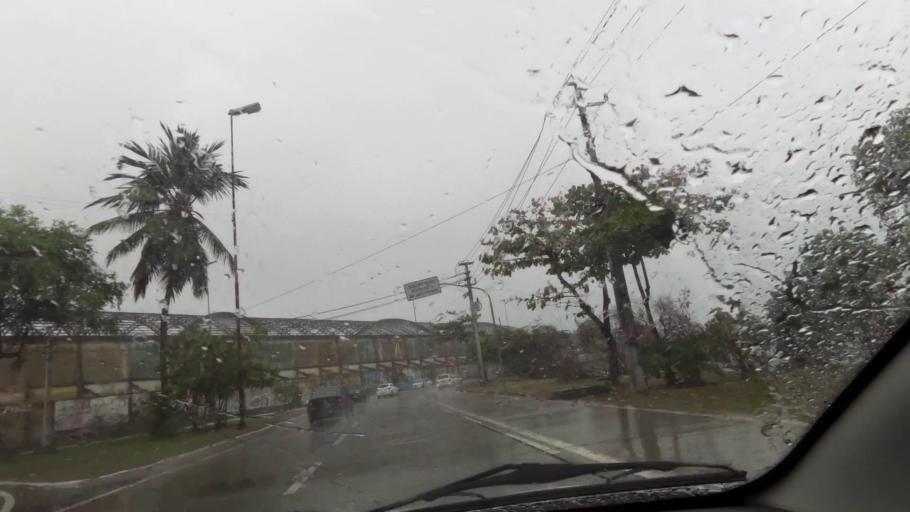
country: BR
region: Pernambuco
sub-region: Recife
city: Recife
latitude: -8.0775
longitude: -34.8909
